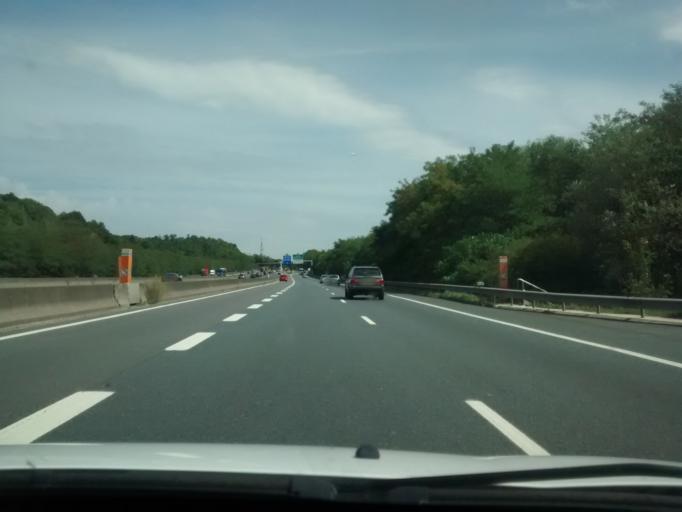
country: FR
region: Ile-de-France
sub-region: Departement de l'Essonne
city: Les Ulis
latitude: 48.6637
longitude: 2.1892
